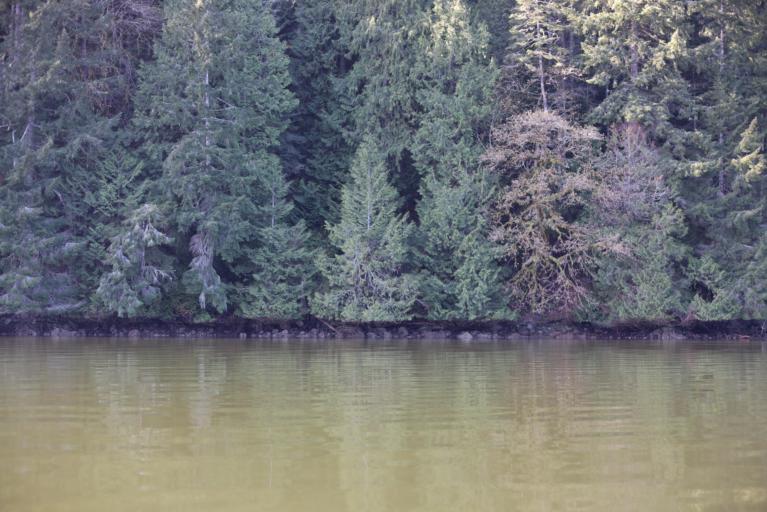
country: CA
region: British Columbia
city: Langford
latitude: 48.5582
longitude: -123.4710
